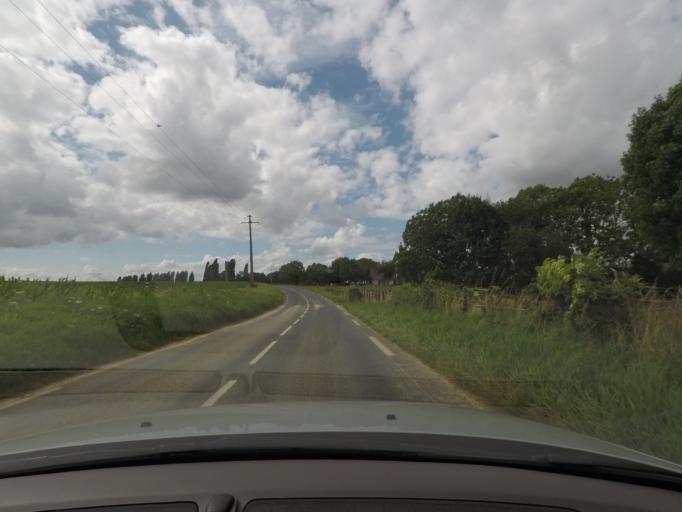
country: FR
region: Haute-Normandie
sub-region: Departement de l'Eure
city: Les Andelys
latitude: 49.2358
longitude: 1.4282
